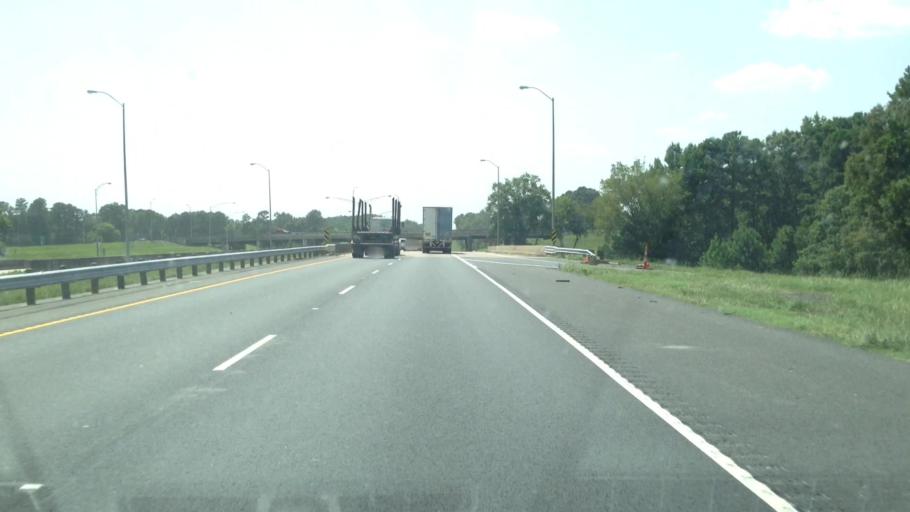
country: US
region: Louisiana
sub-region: Webster Parish
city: Minden
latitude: 32.5890
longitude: -93.2904
